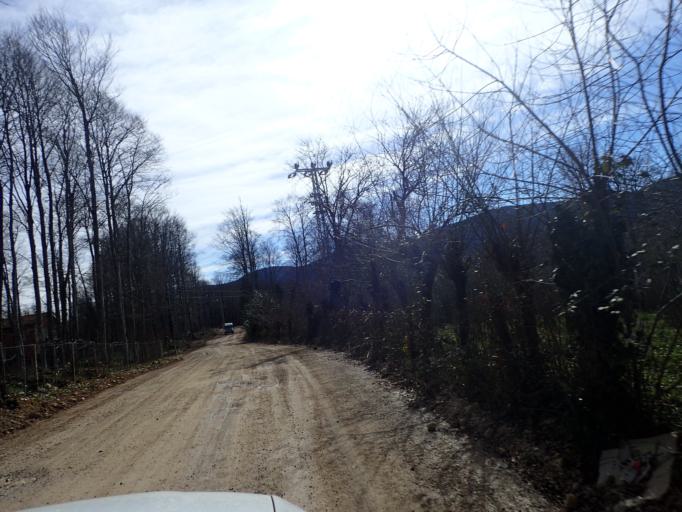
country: TR
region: Ordu
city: Kumru
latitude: 40.9350
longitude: 37.2565
